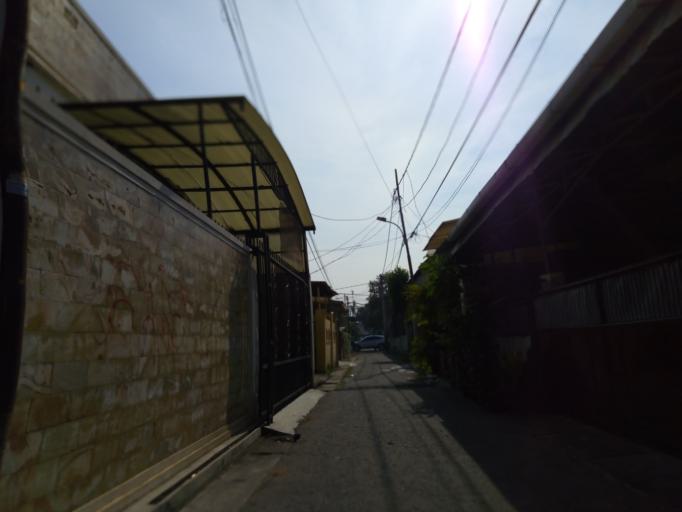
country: ID
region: Jakarta Raya
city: Jakarta
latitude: -6.2104
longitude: 106.8361
